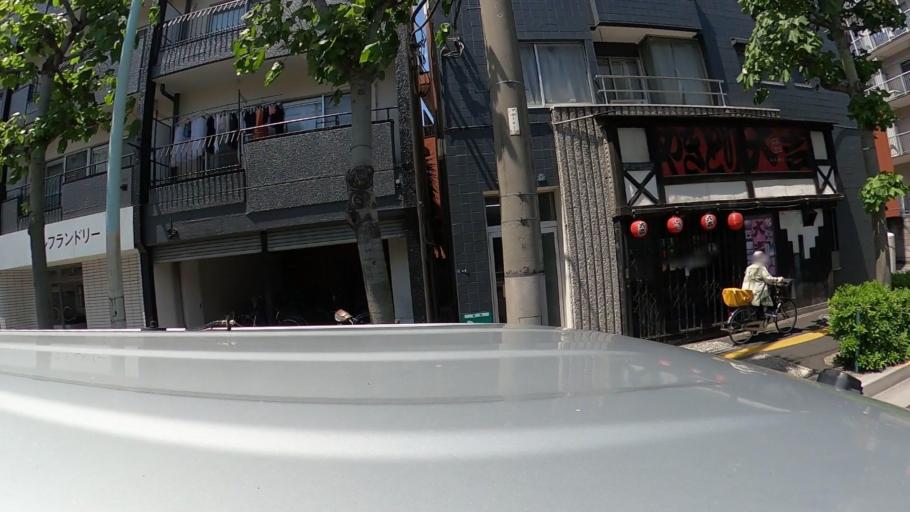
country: JP
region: Kanagawa
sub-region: Kawasaki-shi
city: Kawasaki
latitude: 35.5709
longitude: 139.7347
